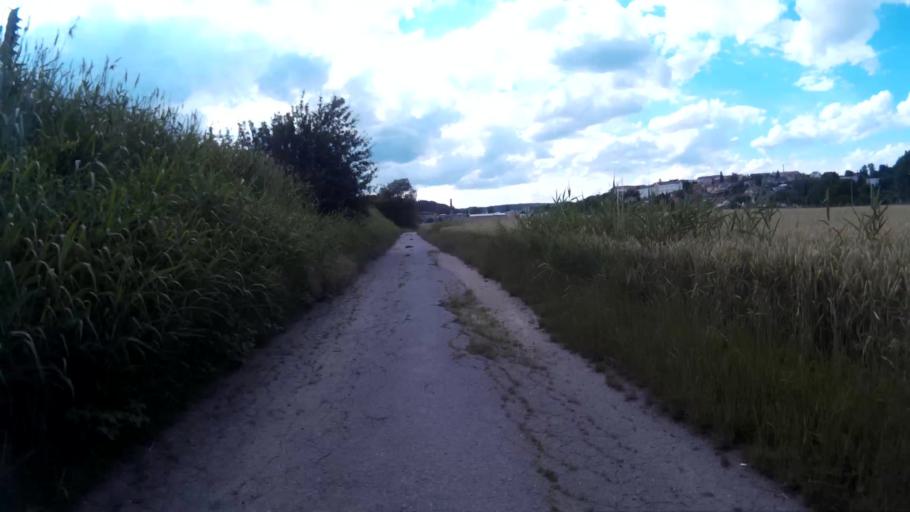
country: CZ
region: South Moravian
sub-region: Okres Brno-Venkov
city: Rosice
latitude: 49.1756
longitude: 16.3956
